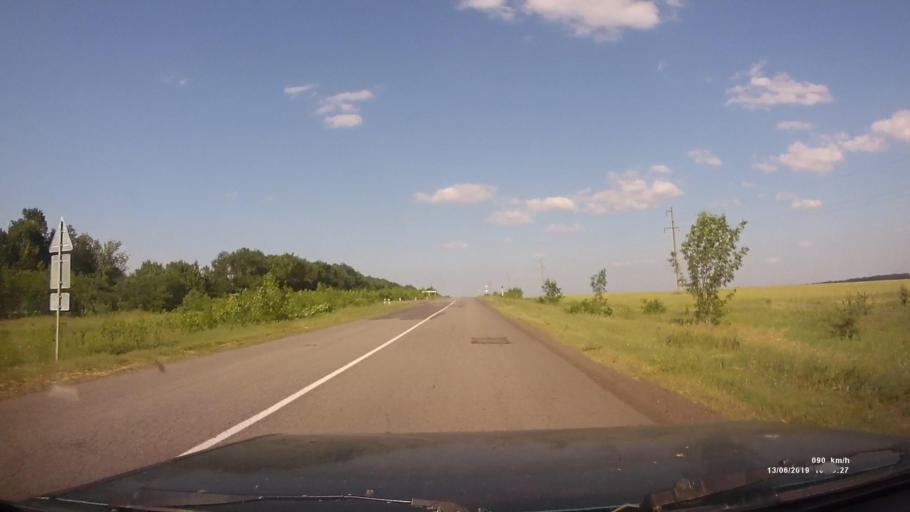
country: RU
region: Rostov
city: Kazanskaya
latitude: 49.9275
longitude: 41.3404
